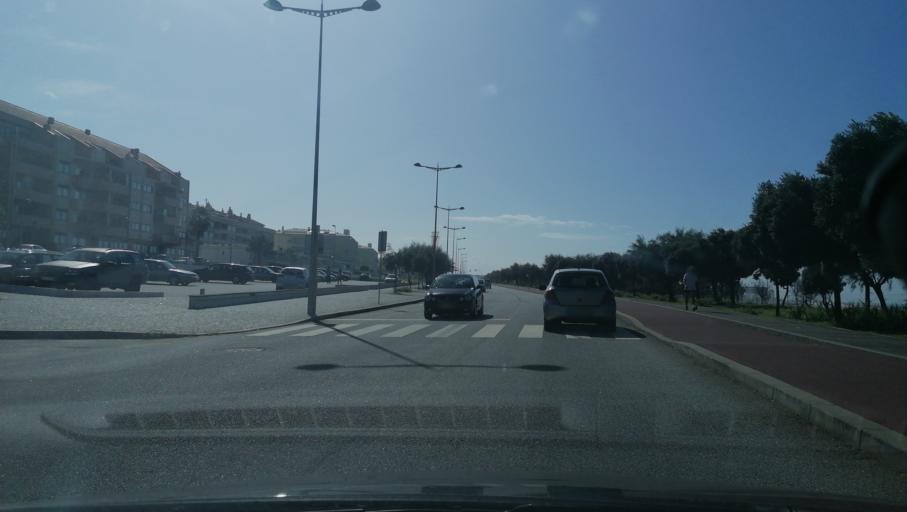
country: PT
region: Aveiro
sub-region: Espinho
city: Espinho
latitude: 41.0250
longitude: -8.6429
